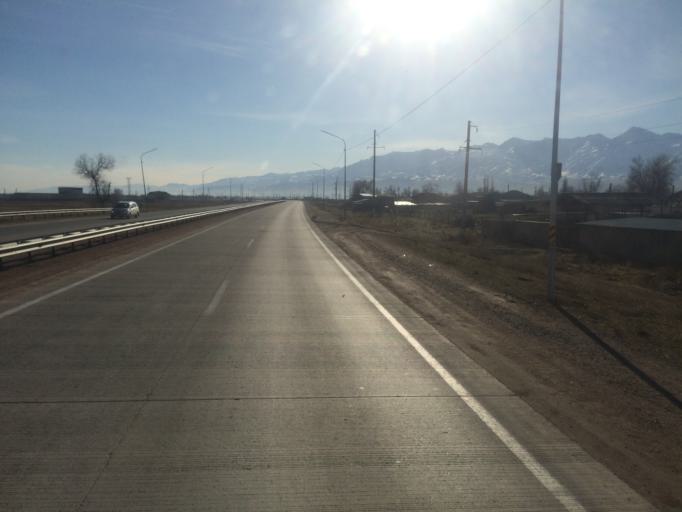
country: KG
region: Talas
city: Ivanovo-Alekseyevka
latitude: 42.9939
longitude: 72.1098
